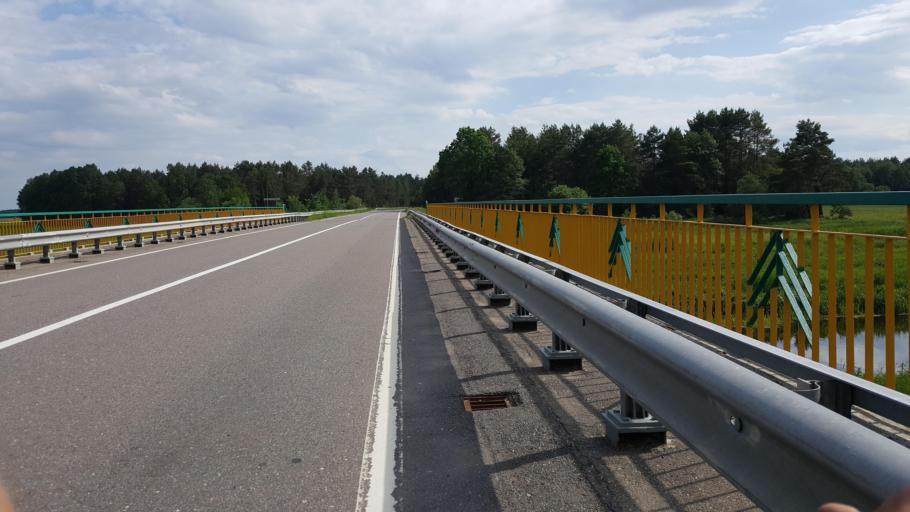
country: BY
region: Brest
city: Zhabinka
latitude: 52.4731
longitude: 24.1549
